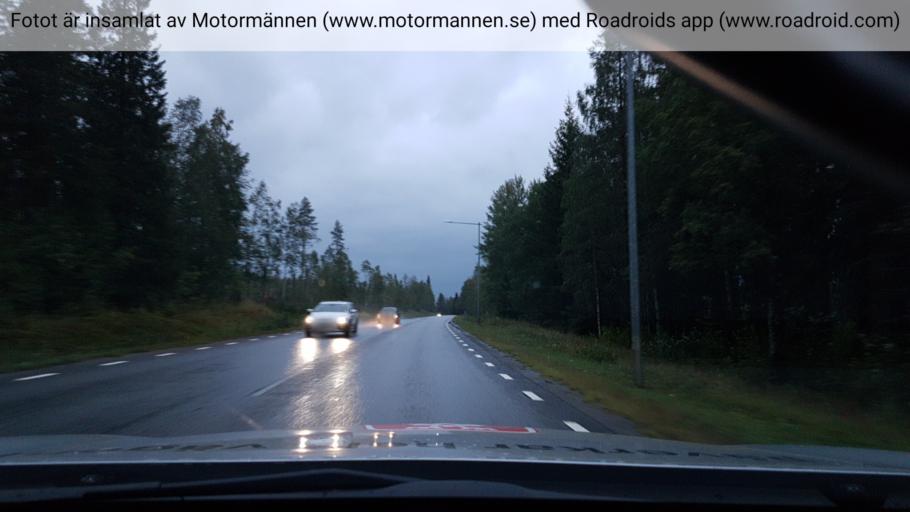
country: SE
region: Vaesterbotten
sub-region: Umea Kommun
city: Ersmark
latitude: 63.8573
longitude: 20.2982
